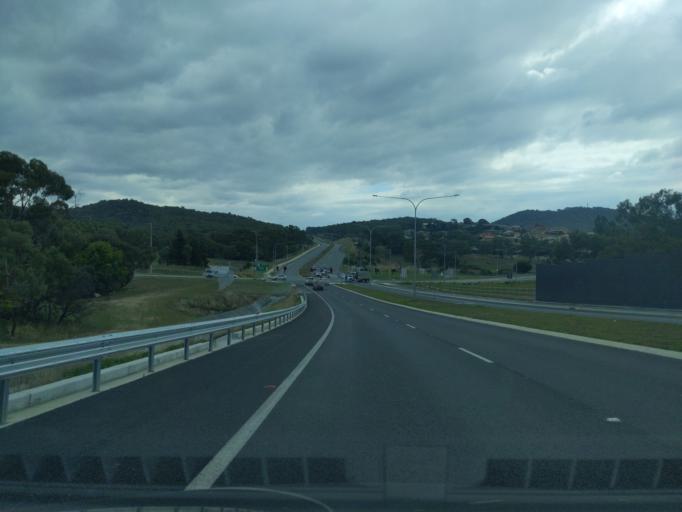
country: AU
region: New South Wales
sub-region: Queanbeyan
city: Queanbeyan
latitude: -35.3786
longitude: 149.2380
